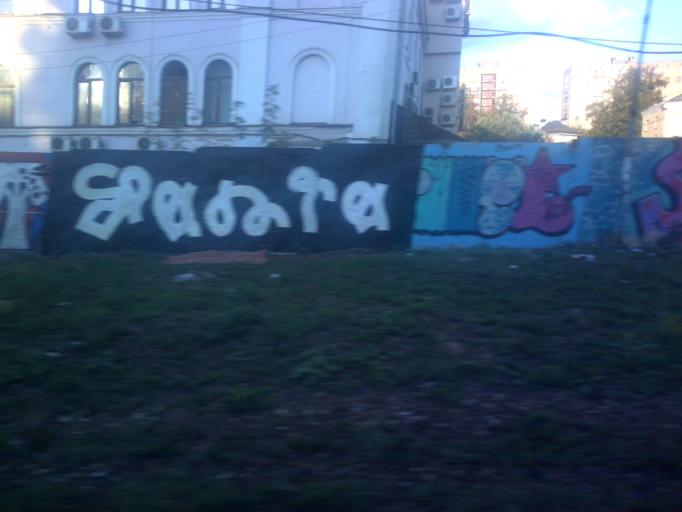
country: RU
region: Moscow
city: Sokol'niki
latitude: 55.7705
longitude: 37.6547
